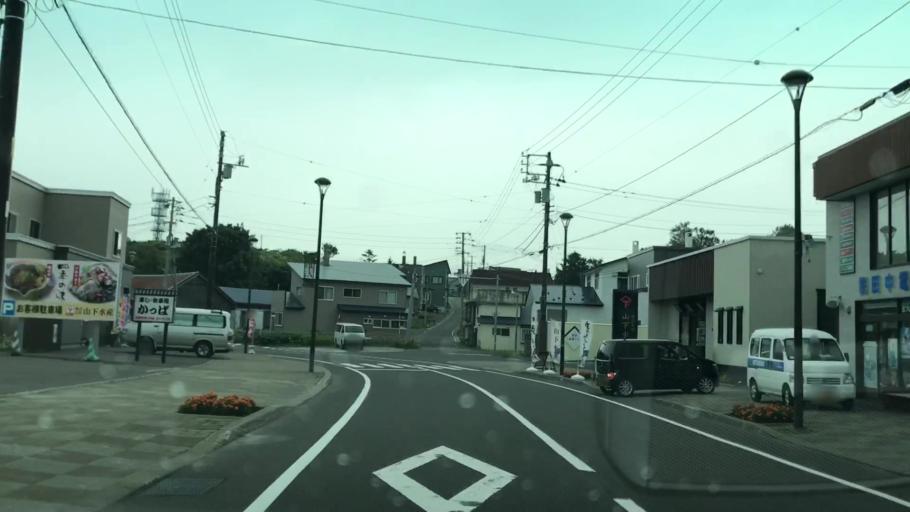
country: JP
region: Hokkaido
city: Iwanai
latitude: 42.7935
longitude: 140.2336
